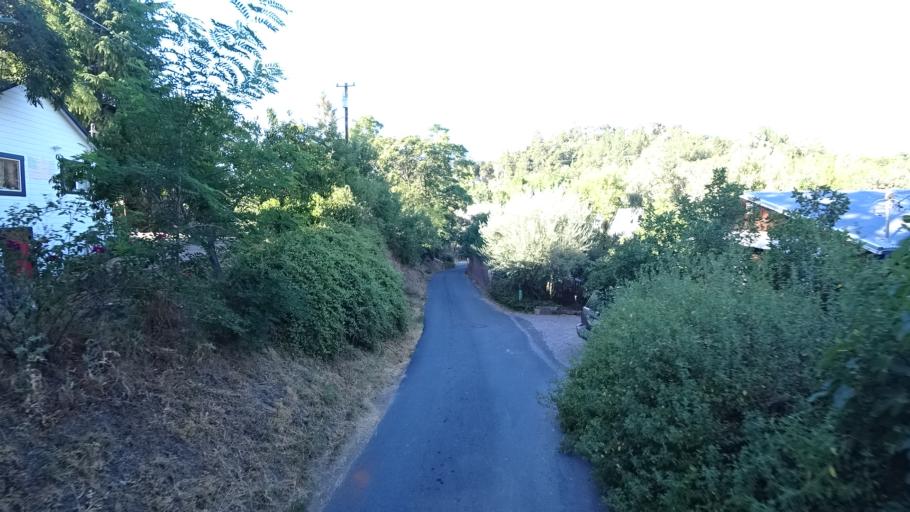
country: US
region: California
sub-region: Amador County
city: Jackson
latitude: 38.3012
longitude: -120.7066
